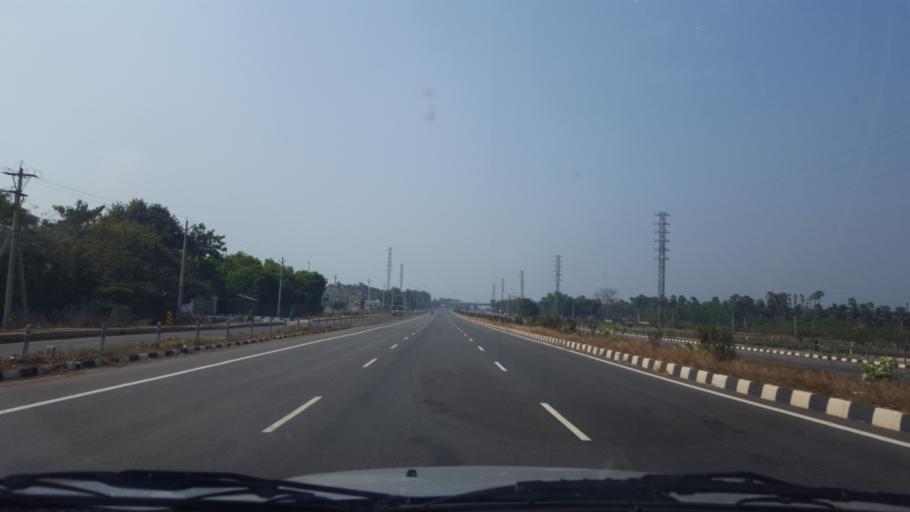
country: IN
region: Andhra Pradesh
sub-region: Vishakhapatnam
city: Bhimunipatnam
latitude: 18.0016
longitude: 83.4768
